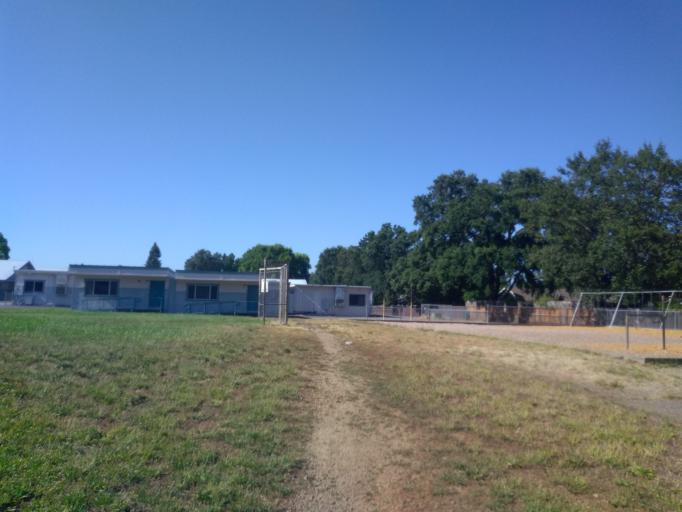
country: US
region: California
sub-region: Mendocino County
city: Ukiah
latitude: 39.1323
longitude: -123.2118
